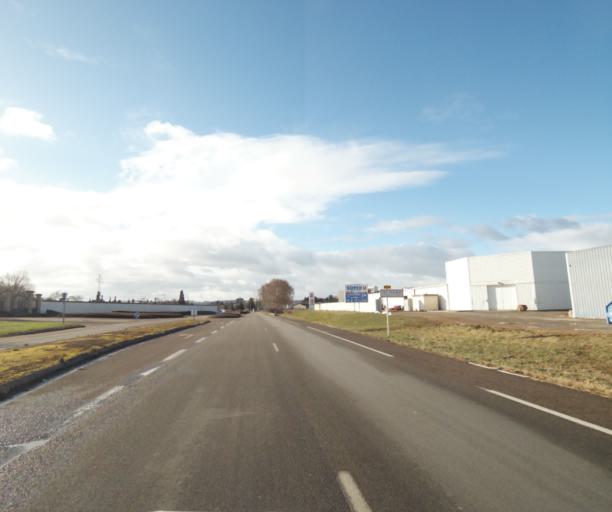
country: FR
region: Rhone-Alpes
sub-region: Departement de la Loire
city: Le Coteau
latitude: 46.0293
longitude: 4.0983
